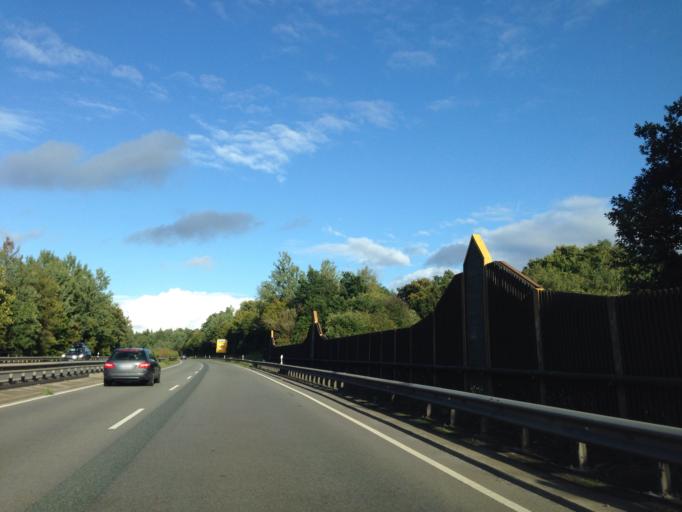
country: DE
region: Lower Saxony
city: Deutsch Evern
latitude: 53.2093
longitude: 10.4302
